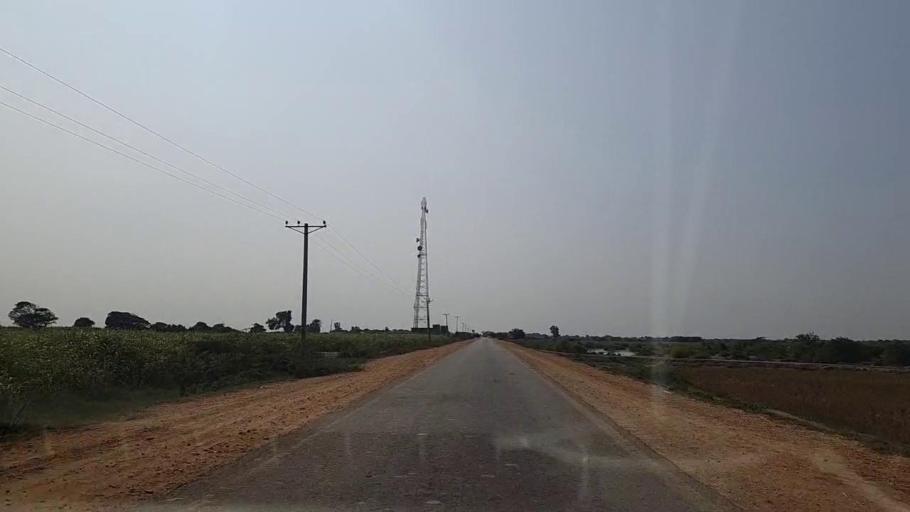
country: PK
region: Sindh
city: Chuhar Jamali
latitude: 24.2857
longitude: 67.9229
